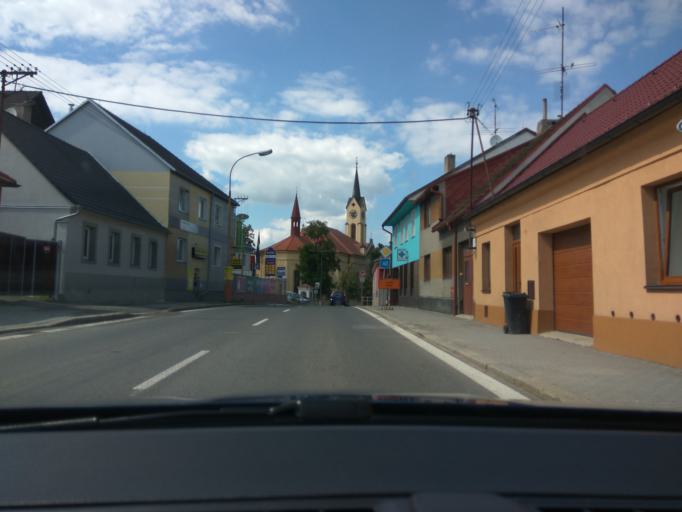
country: CZ
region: Jihocesky
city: Milevsko
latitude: 49.4483
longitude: 14.3598
